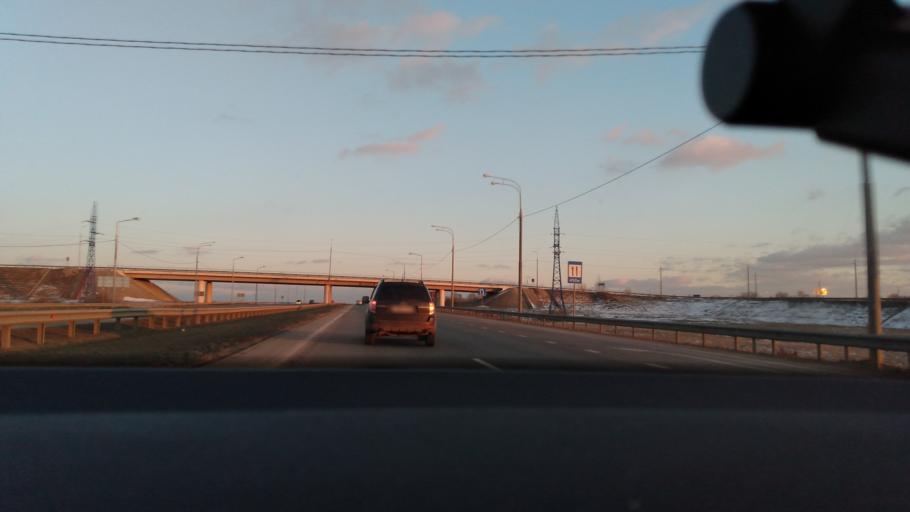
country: RU
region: Moskovskaya
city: Kolomna
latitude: 55.1215
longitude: 38.8154
